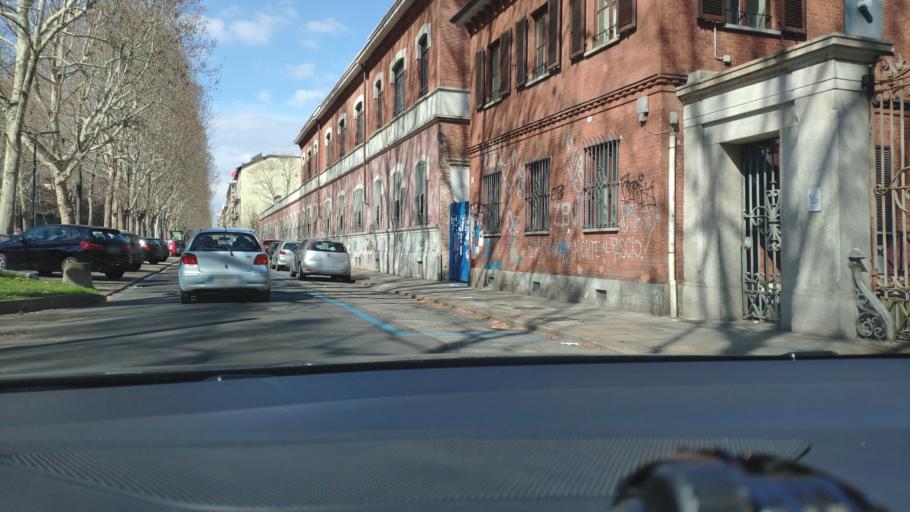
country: IT
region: Piedmont
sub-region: Provincia di Torino
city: Turin
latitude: 45.0720
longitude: 7.6986
